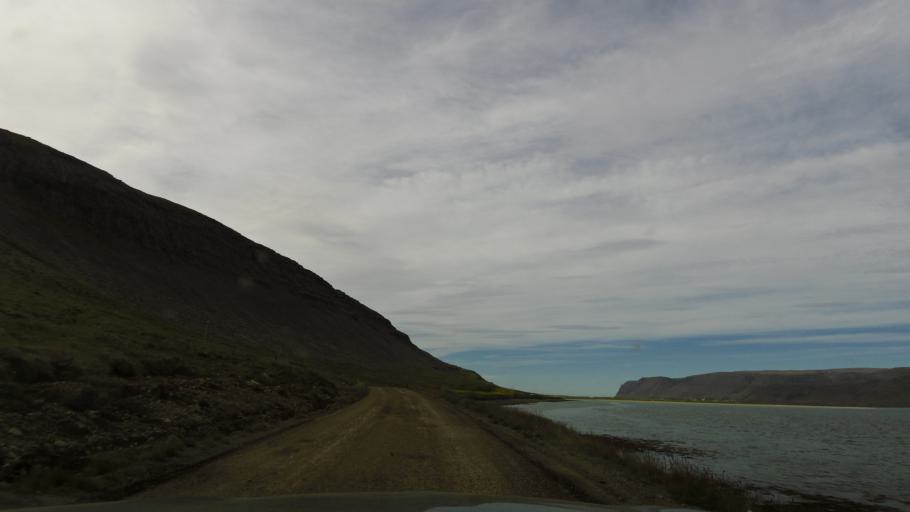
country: IS
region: West
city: Olafsvik
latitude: 65.5399
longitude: -23.9328
